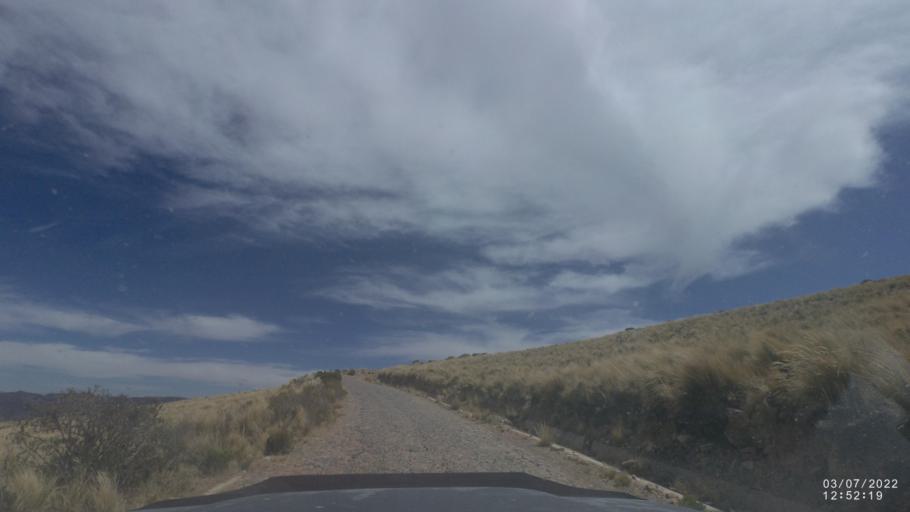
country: BO
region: Cochabamba
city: Irpa Irpa
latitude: -17.7492
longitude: -66.6605
